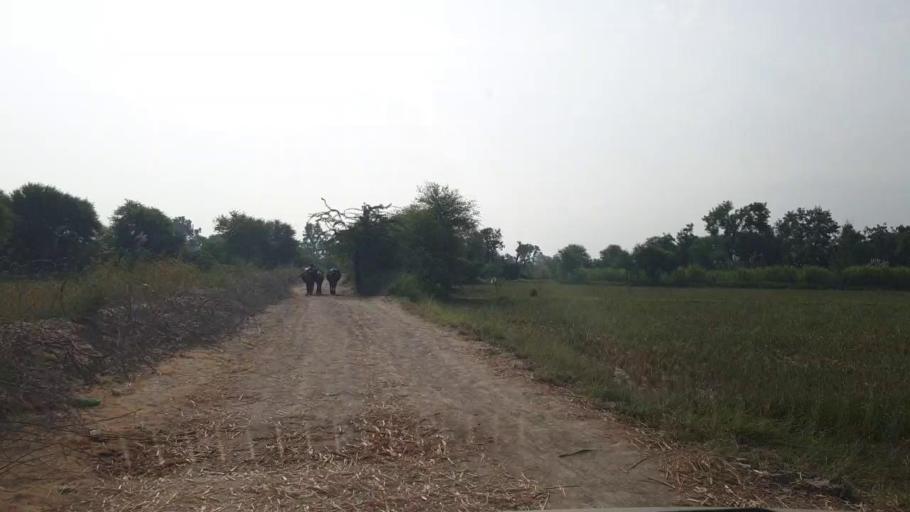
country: PK
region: Sindh
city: Rajo Khanani
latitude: 24.9059
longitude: 68.9210
